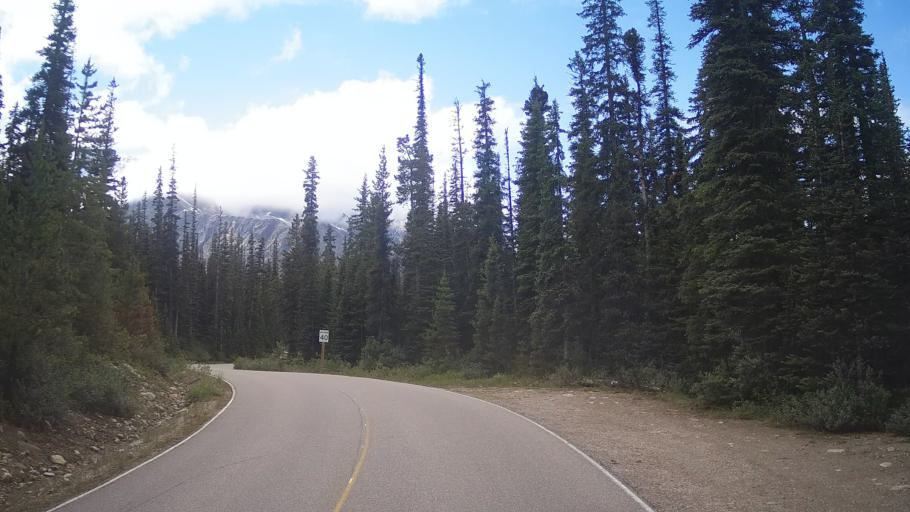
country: CA
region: Alberta
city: Jasper Park Lodge
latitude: 52.7183
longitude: -118.0534
